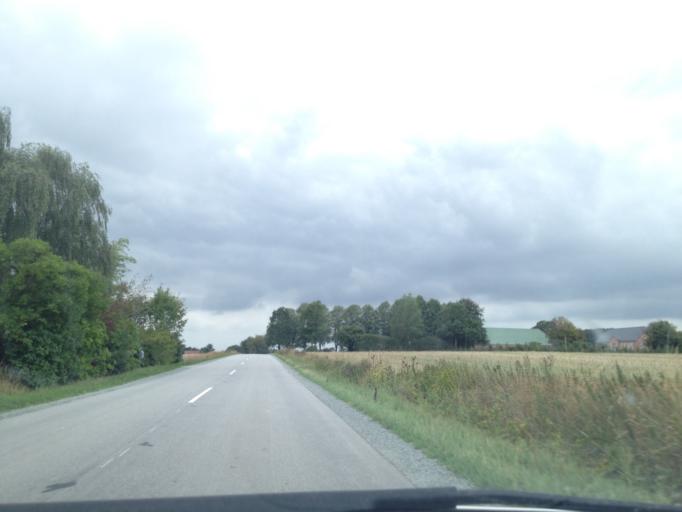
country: DK
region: South Denmark
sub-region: Haderslev Kommune
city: Starup
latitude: 55.3066
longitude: 9.5361
